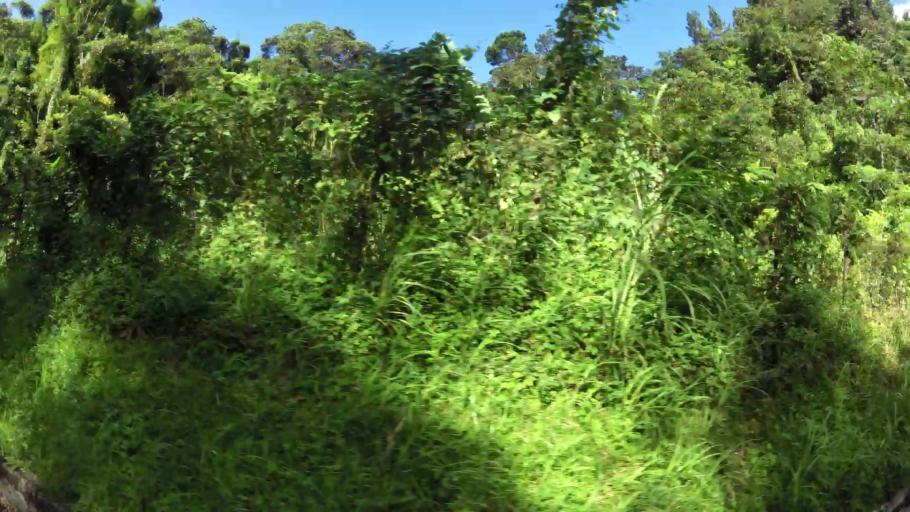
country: MQ
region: Martinique
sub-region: Martinique
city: Saint-Joseph
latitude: 14.6756
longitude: -61.0920
